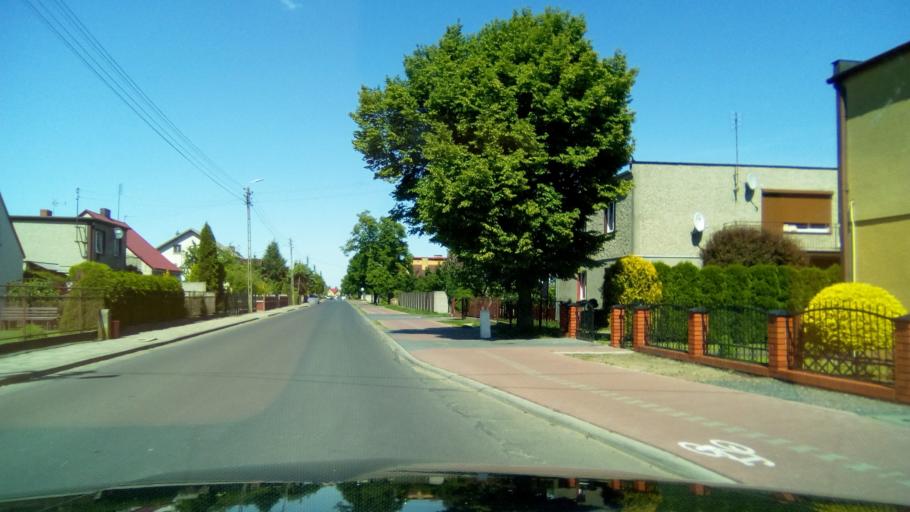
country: PL
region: Greater Poland Voivodeship
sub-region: Powiat gnieznienski
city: Niechanowo
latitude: 52.4656
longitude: 17.6789
